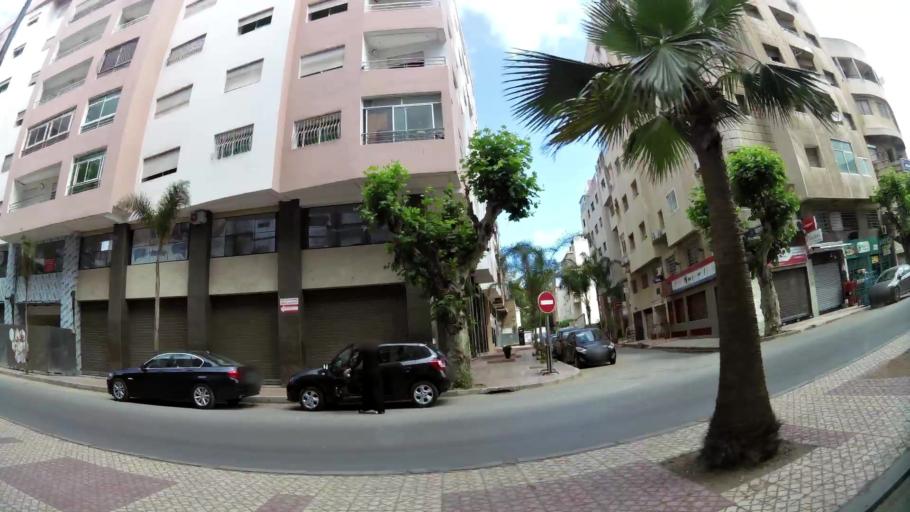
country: MA
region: Gharb-Chrarda-Beni Hssen
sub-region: Kenitra Province
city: Kenitra
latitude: 34.2612
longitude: -6.5863
